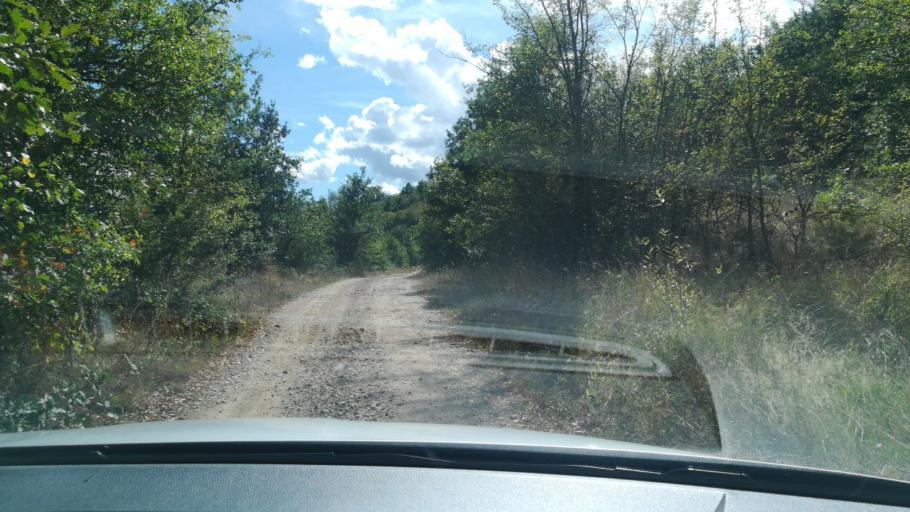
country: MK
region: Delcevo
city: Delcevo
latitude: 41.8986
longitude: 22.8053
